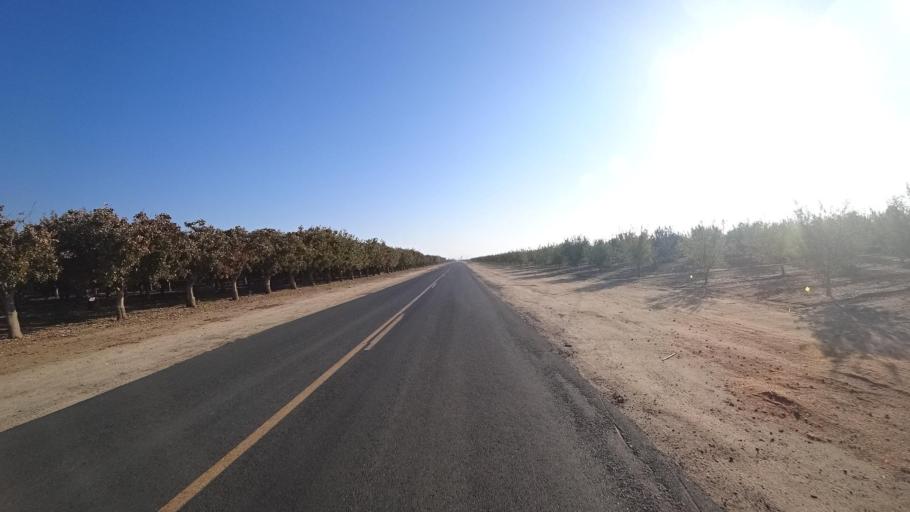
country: US
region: California
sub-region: Kern County
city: Delano
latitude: 35.7687
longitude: -119.2183
